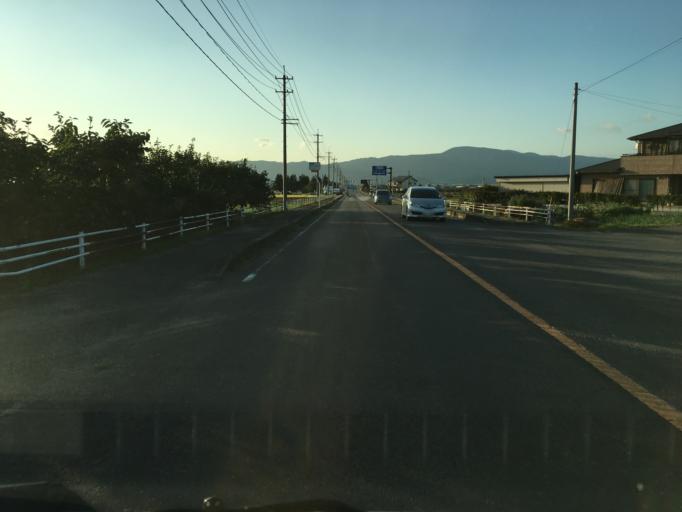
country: JP
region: Fukushima
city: Hobaramachi
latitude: 37.8086
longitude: 140.5691
